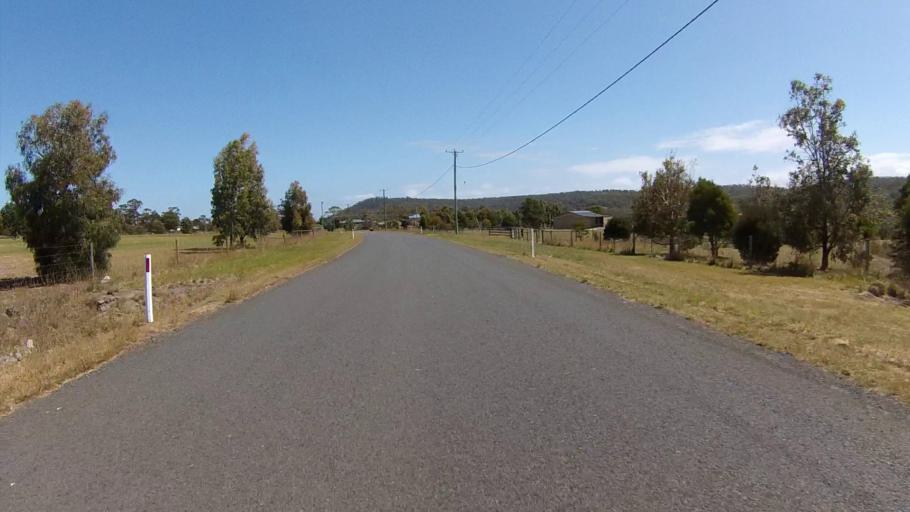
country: AU
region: Tasmania
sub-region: Clarence
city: Sandford
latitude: -42.9550
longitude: 147.4848
